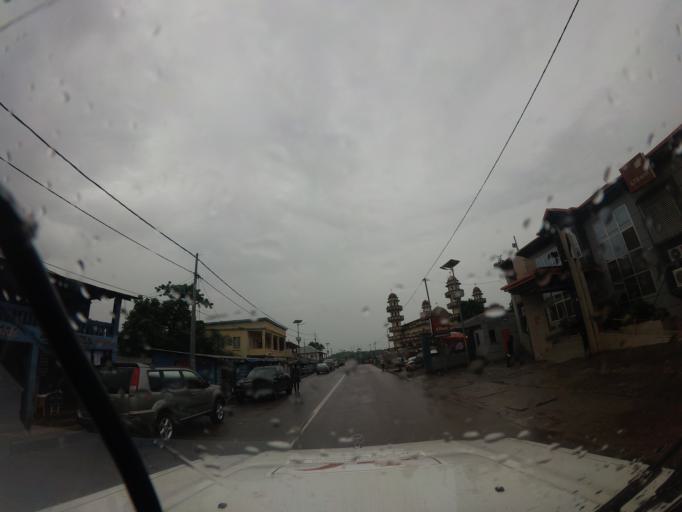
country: SL
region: Northern Province
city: Makeni
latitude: 8.8876
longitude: -12.0446
